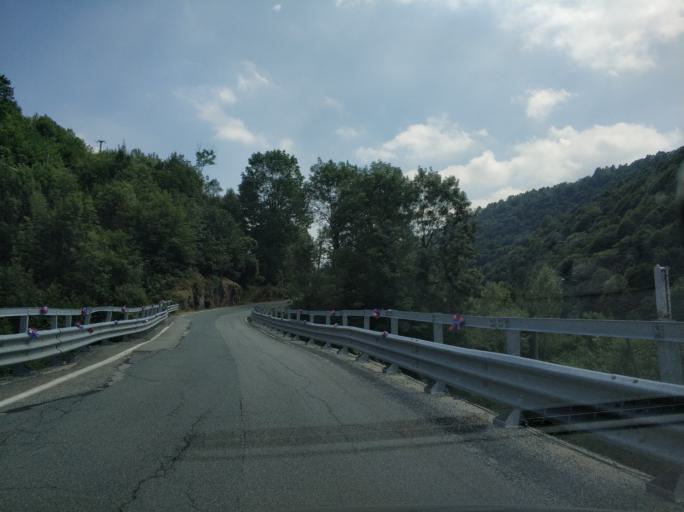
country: IT
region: Piedmont
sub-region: Provincia di Torino
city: Ceres
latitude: 45.3078
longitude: 7.3931
